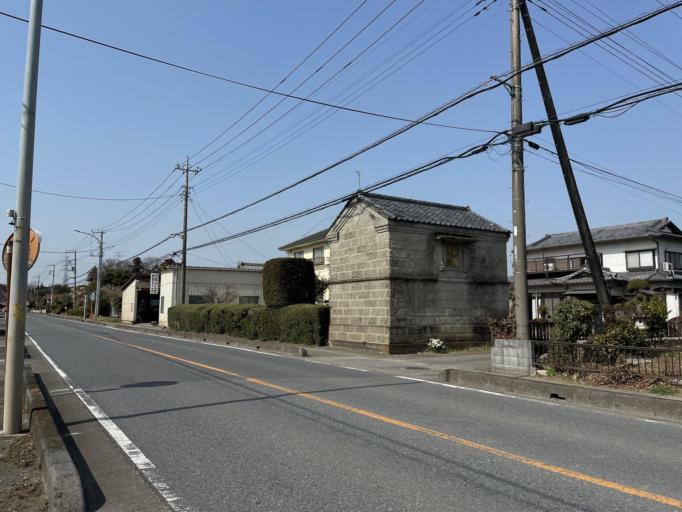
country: JP
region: Saitama
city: Ogawa
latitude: 36.1038
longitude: 139.2668
